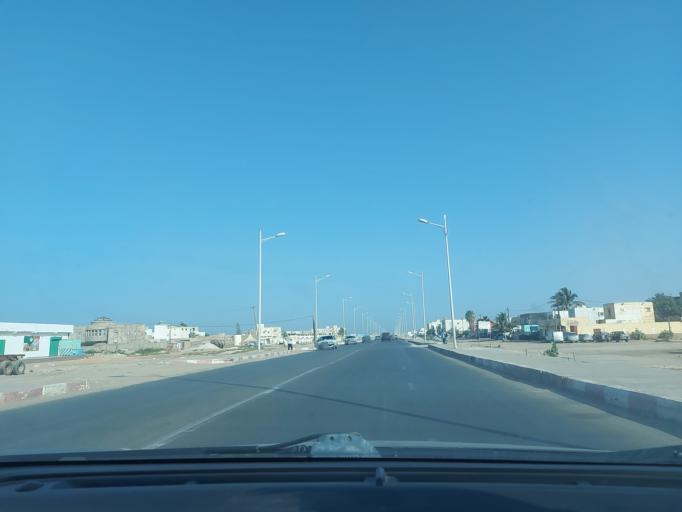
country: MR
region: Nouakchott
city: Nouakchott
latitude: 18.0921
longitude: -16.0111
